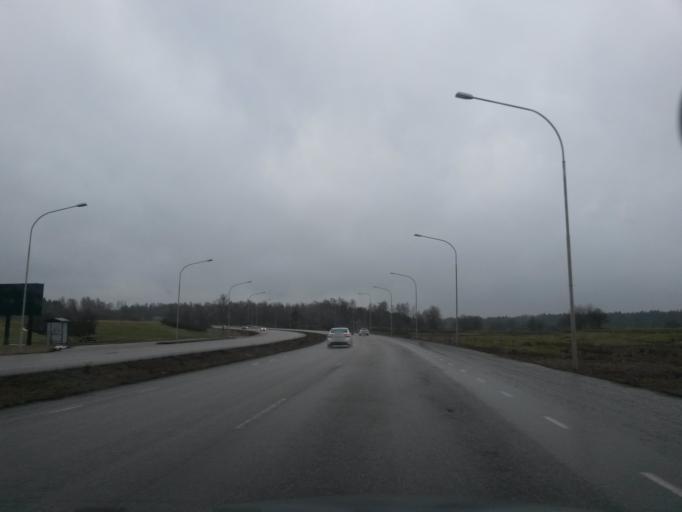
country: SE
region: Vaestra Goetaland
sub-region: Vanersborgs Kommun
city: Vanersborg
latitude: 58.3630
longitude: 12.3136
